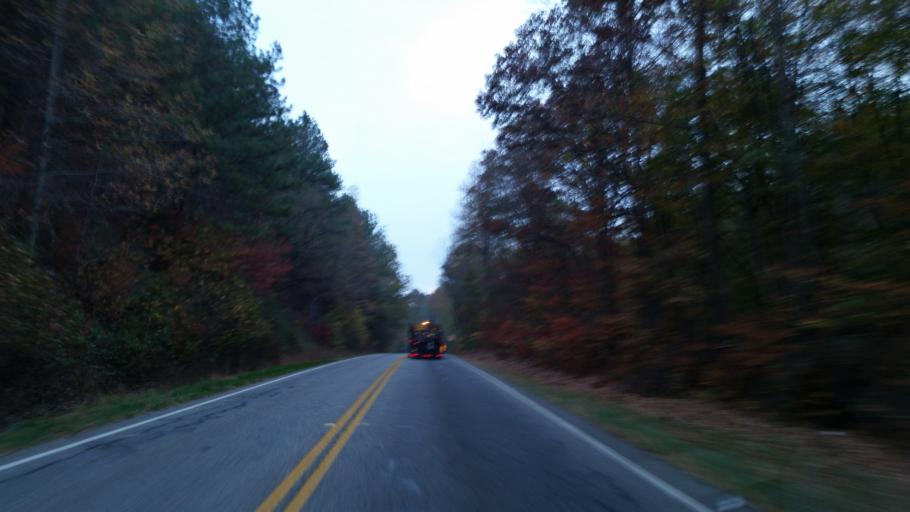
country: US
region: Georgia
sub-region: Gilmer County
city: Ellijay
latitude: 34.5802
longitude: -84.6496
